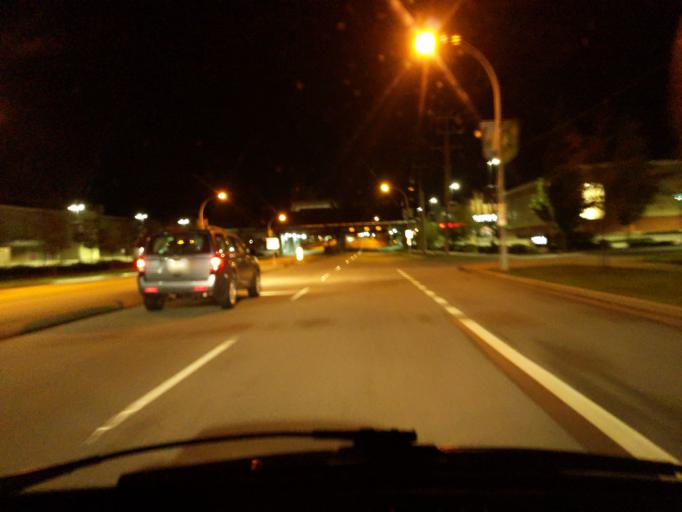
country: CA
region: British Columbia
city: Surrey
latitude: 49.1916
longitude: -122.8015
